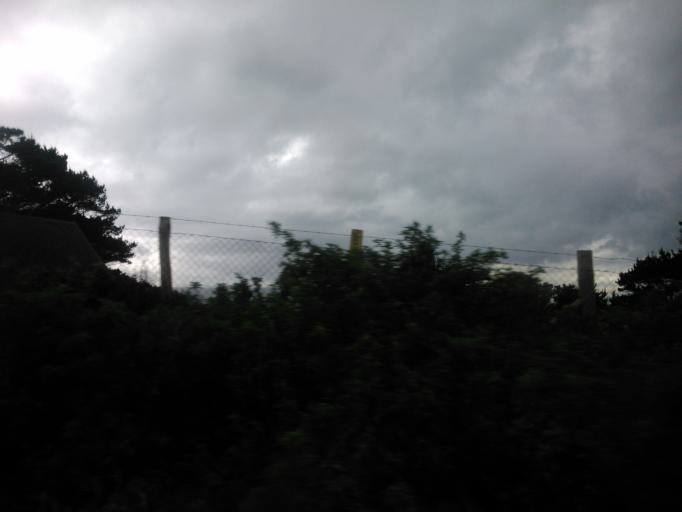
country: CL
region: Araucania
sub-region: Provincia de Cautin
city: Carahue
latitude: -38.8153
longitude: -73.3974
